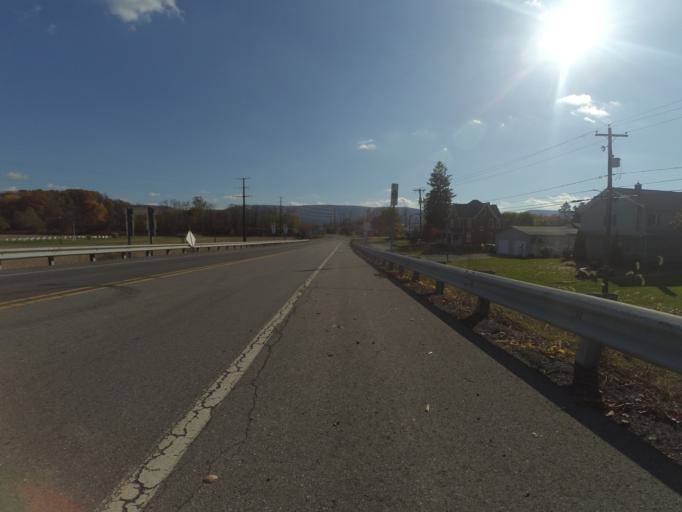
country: US
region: Pennsylvania
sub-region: Clinton County
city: Avis
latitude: 41.1955
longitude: -77.2969
